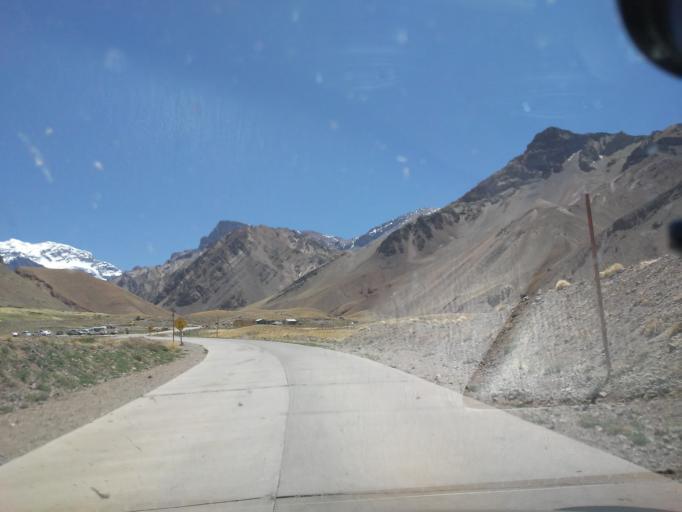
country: CL
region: Valparaiso
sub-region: Provincia de Los Andes
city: Los Andes
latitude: -32.8135
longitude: -69.9421
